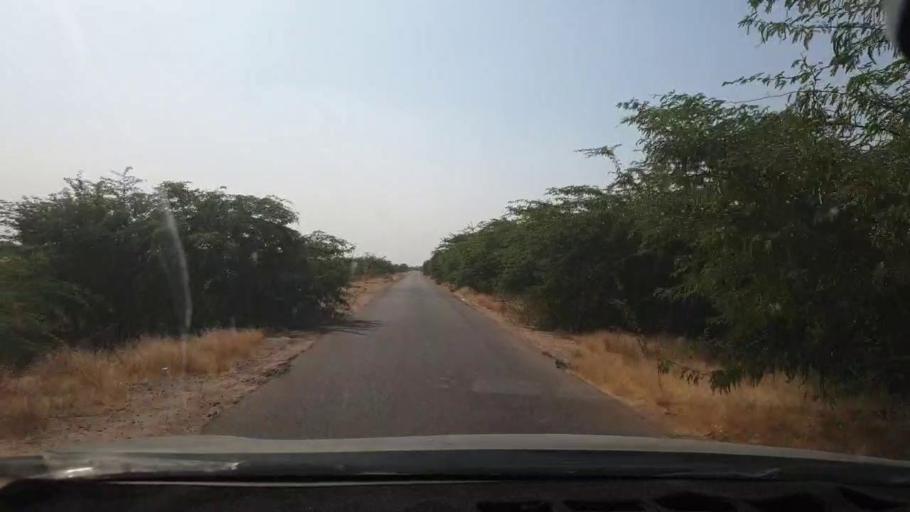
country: PK
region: Sindh
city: Malir Cantonment
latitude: 25.1056
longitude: 67.1995
